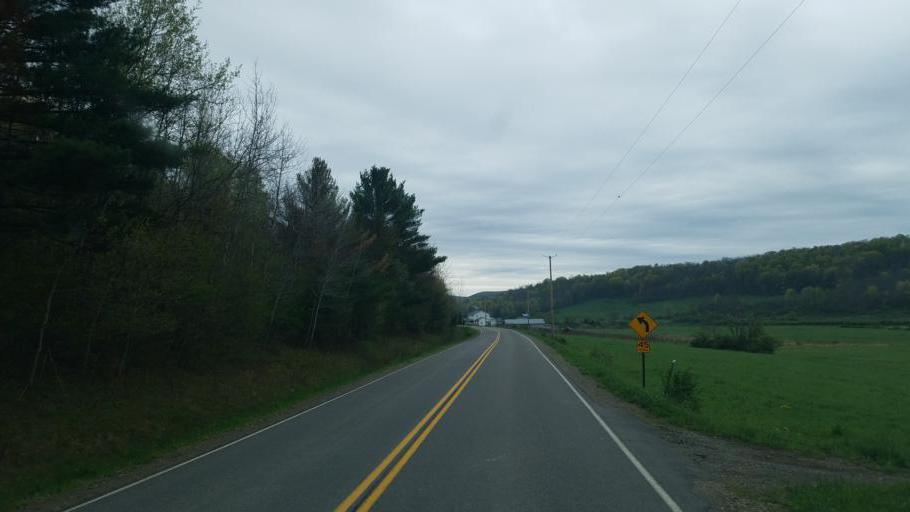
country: US
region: Pennsylvania
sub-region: Tioga County
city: Westfield
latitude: 42.0143
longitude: -77.4733
